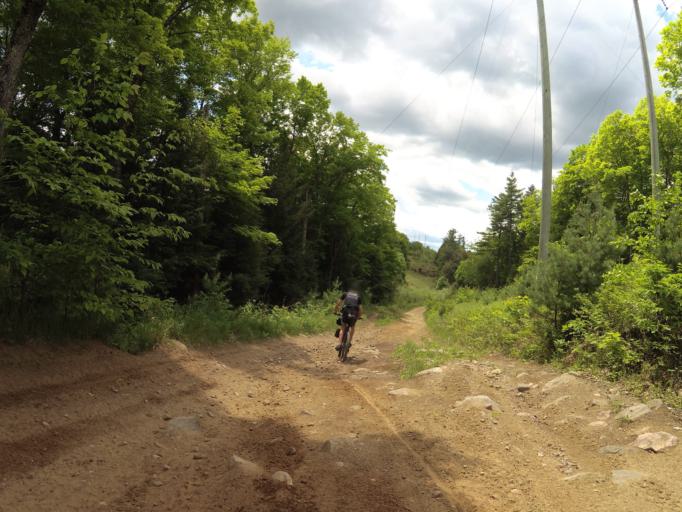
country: CA
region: Ontario
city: Renfrew
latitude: 45.0640
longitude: -76.8586
